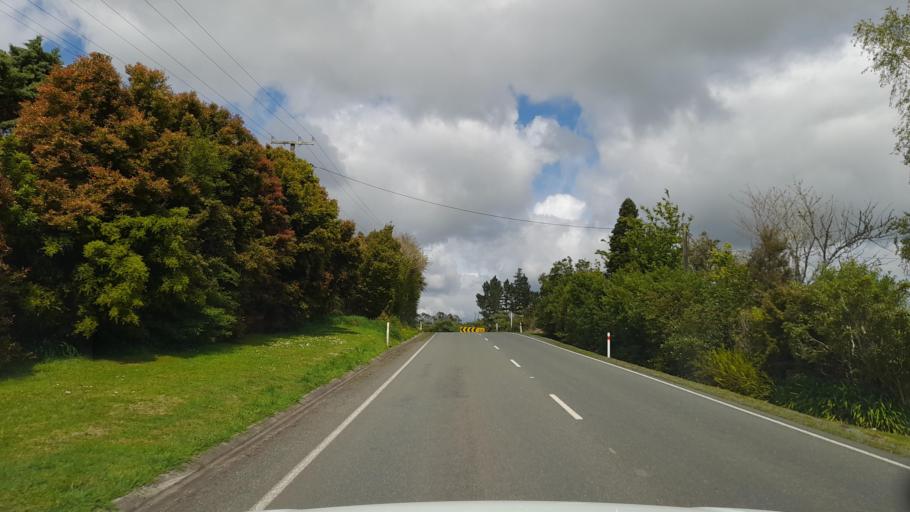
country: NZ
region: Northland
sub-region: Whangarei
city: Maungatapere
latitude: -35.6607
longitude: 174.1807
